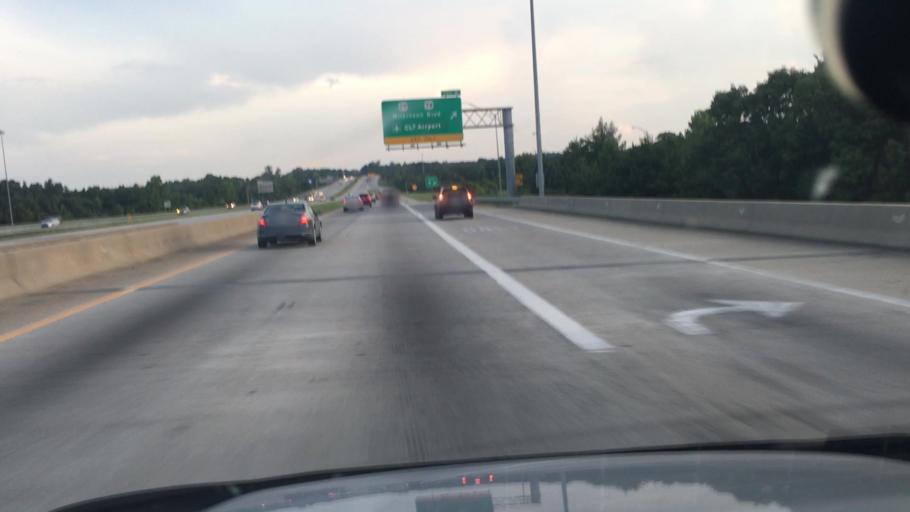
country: US
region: North Carolina
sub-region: Gaston County
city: Belmont
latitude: 35.2398
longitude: -80.9701
